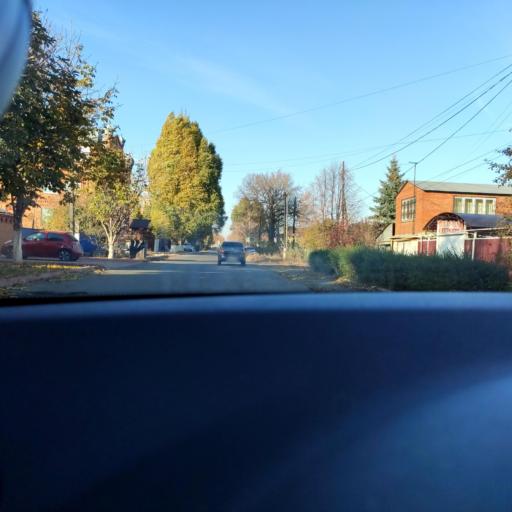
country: RU
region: Samara
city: Petra-Dubrava
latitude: 53.2517
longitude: 50.3287
